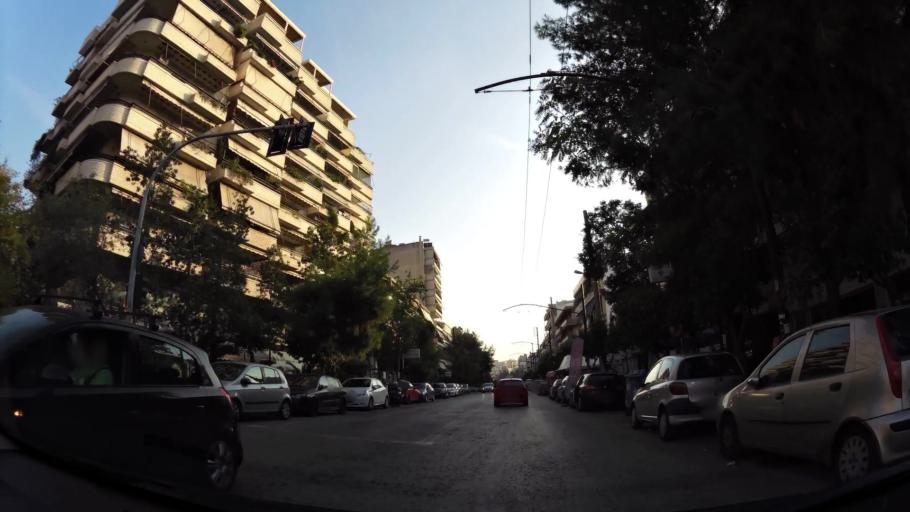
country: GR
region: Attica
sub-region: Nomarchia Athinas
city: Galatsi
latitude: 38.0227
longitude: 23.7541
